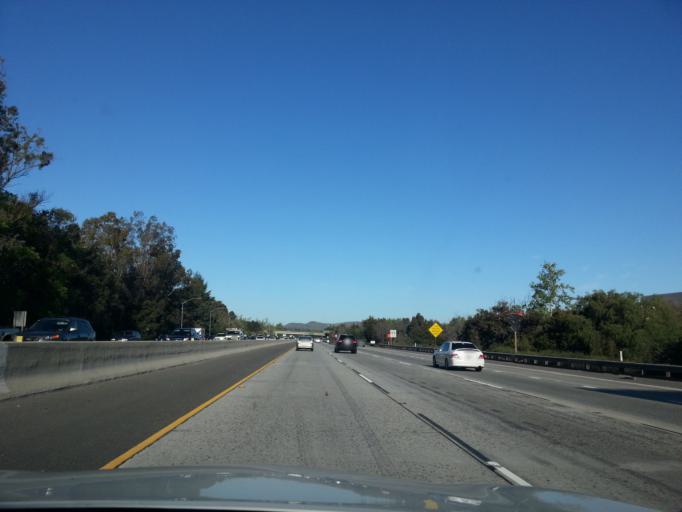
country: US
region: California
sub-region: Ventura County
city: Thousand Oaks
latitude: 34.1803
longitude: -118.8851
